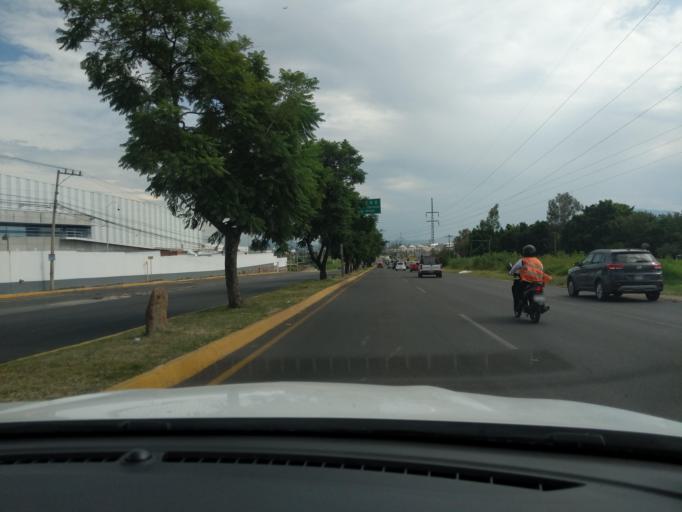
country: MX
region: Jalisco
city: San Jose del Castillo
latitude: 20.5061
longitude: -103.2334
